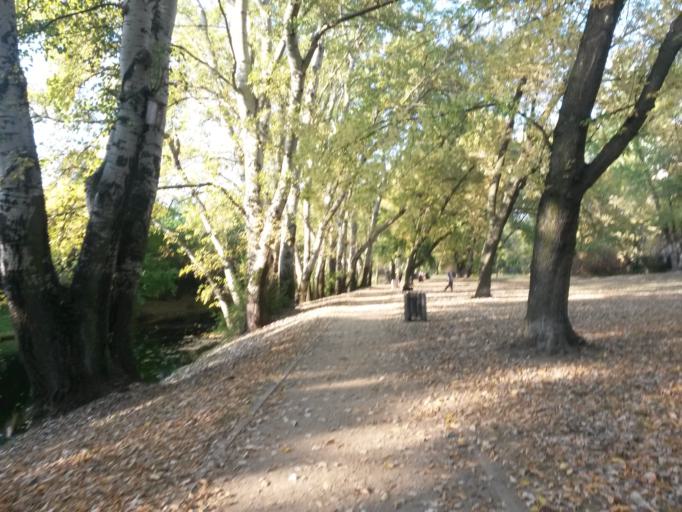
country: PL
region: Masovian Voivodeship
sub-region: Warszawa
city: Mokotow
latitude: 52.1990
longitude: 21.0408
